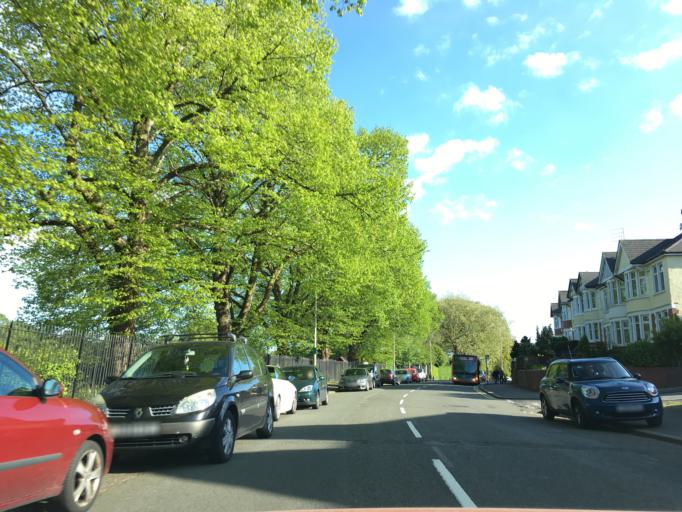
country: GB
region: Wales
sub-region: Cardiff
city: Cardiff
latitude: 51.5074
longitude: -3.1768
